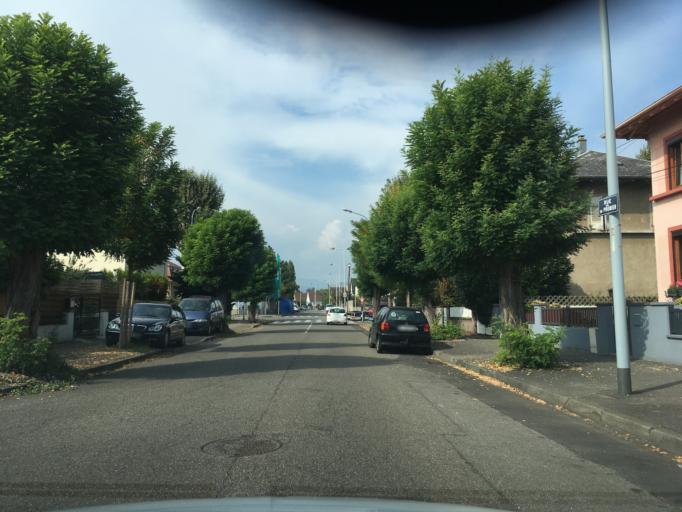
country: FR
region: Alsace
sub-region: Departement du Haut-Rhin
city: Colmar
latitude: 48.0905
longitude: 7.3716
